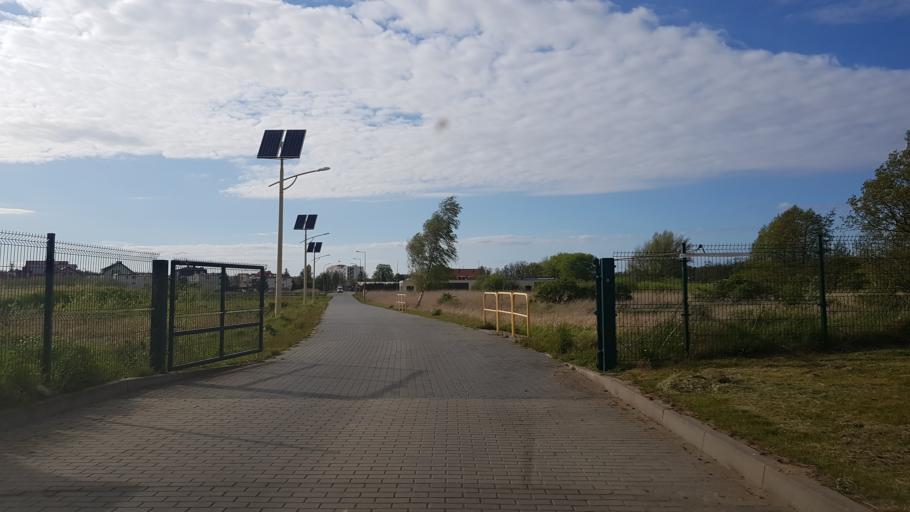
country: PL
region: West Pomeranian Voivodeship
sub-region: Powiat slawienski
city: Darlowo
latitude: 54.4342
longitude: 16.3856
